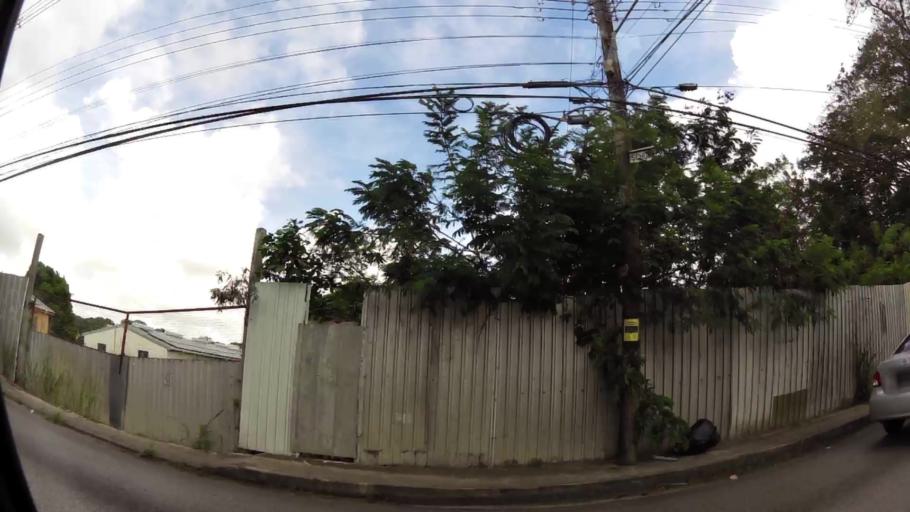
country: BB
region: Saint Michael
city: Bridgetown
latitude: 13.1055
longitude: -59.6059
